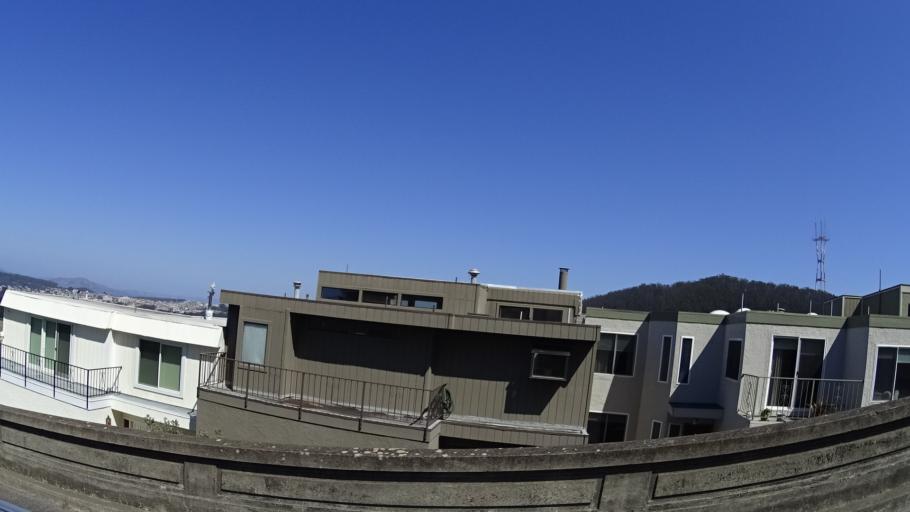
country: US
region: California
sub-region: San Mateo County
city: Daly City
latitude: 37.7568
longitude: -122.4711
